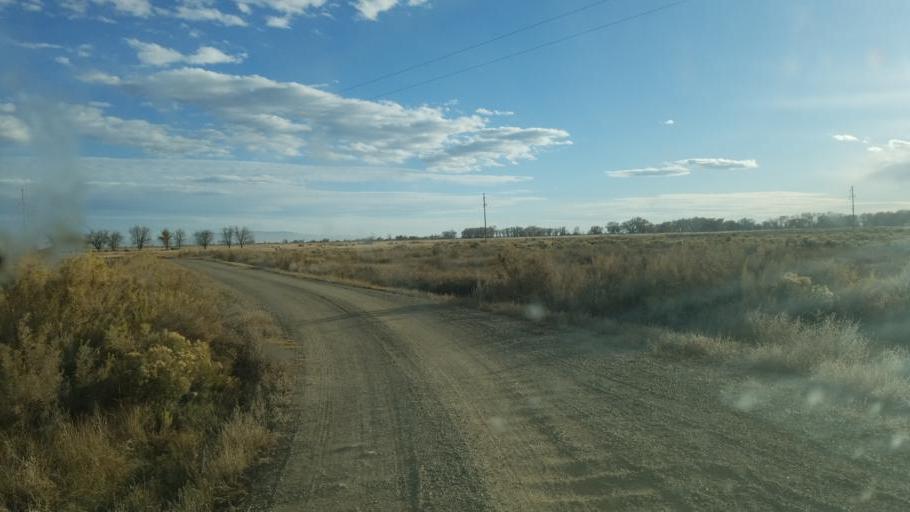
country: US
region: Colorado
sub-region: Alamosa County
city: Alamosa East
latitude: 37.4607
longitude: -105.8344
